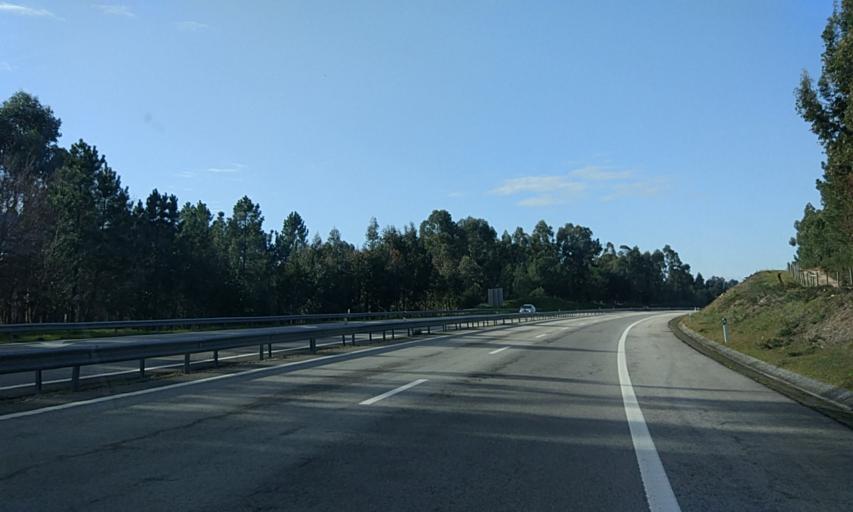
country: PT
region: Viseu
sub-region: Viseu
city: Campo
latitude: 40.7159
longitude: -7.9315
